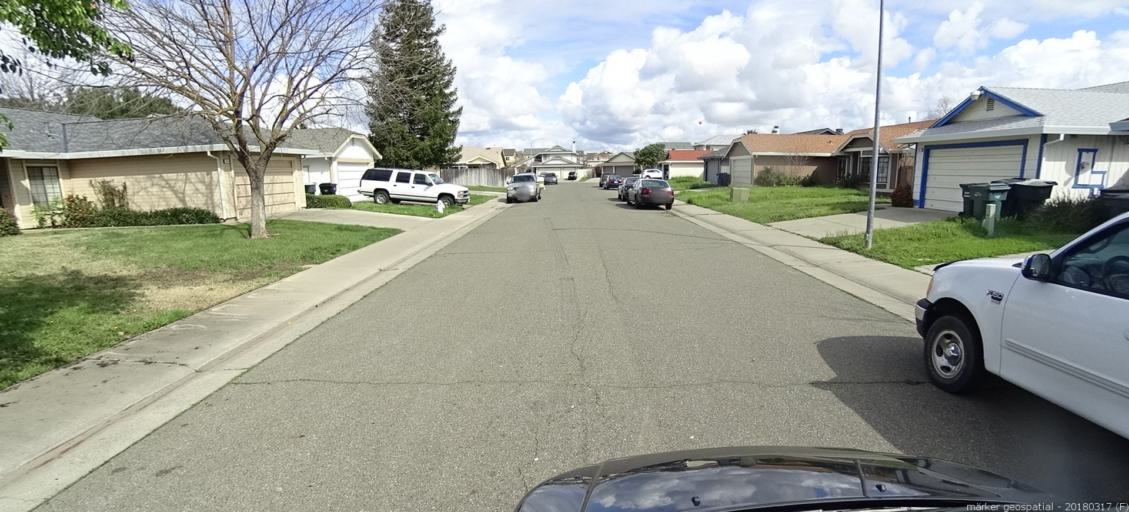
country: US
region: California
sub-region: Sacramento County
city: Florin
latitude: 38.4695
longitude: -121.4063
